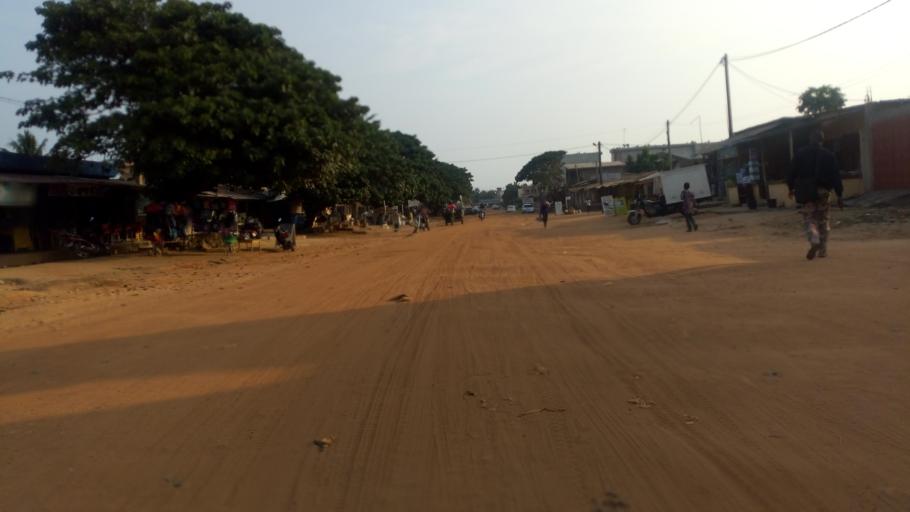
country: TG
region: Maritime
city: Lome
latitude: 6.1963
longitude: 1.1826
